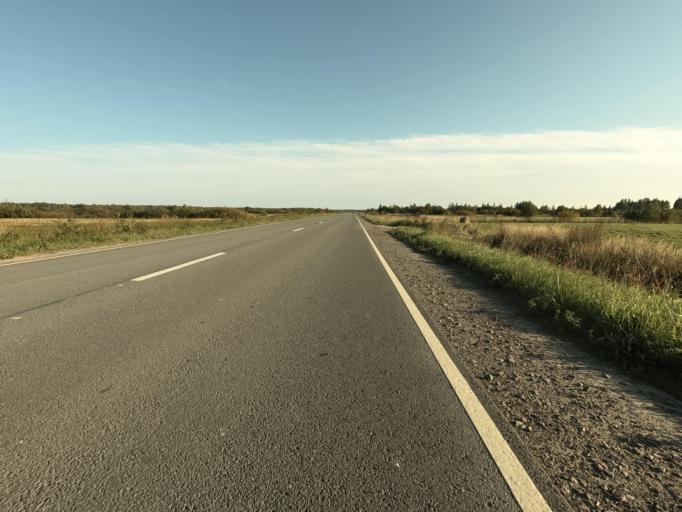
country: RU
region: St.-Petersburg
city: Sapernyy
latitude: 59.7488
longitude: 30.6406
